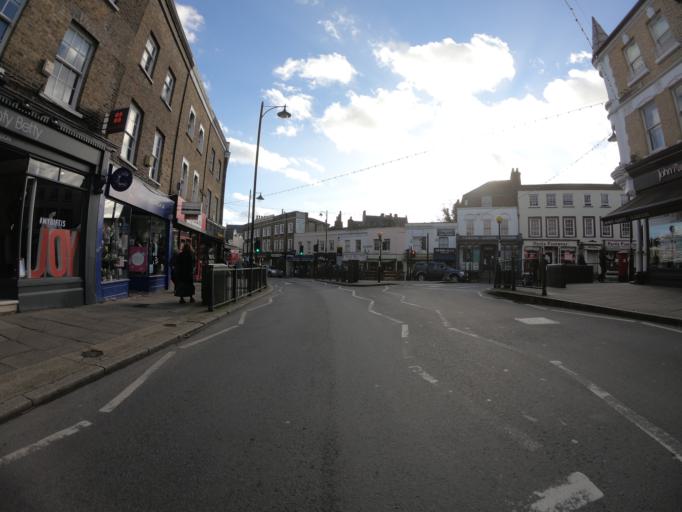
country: GB
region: England
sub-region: Greater London
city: Blackheath
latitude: 51.4665
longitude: 0.0086
